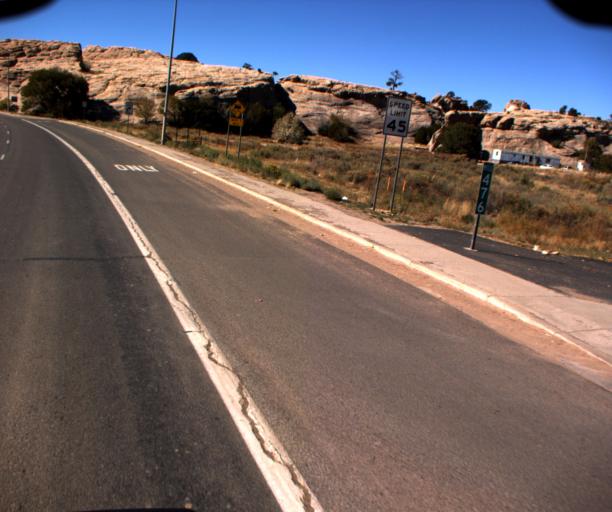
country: US
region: Arizona
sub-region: Apache County
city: Window Rock
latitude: 35.6629
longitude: -109.0476
